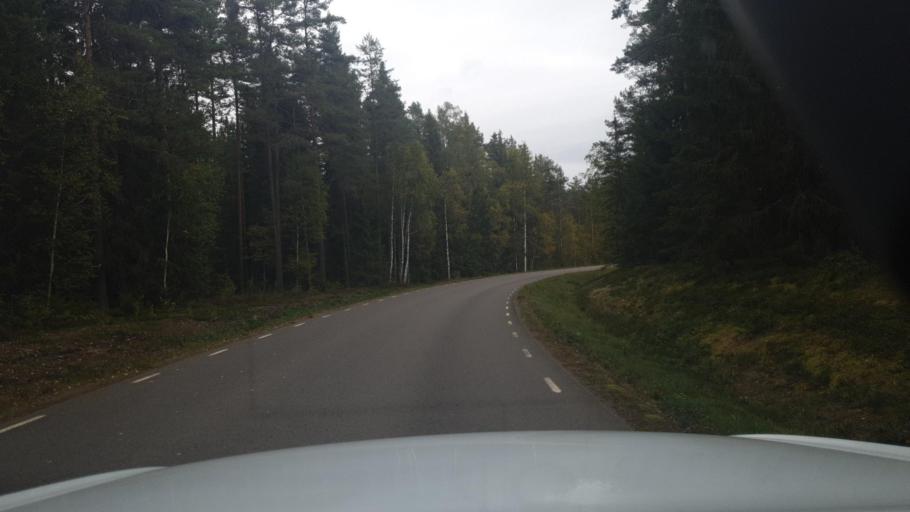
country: SE
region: Vaermland
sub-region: Eda Kommun
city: Charlottenberg
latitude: 60.0158
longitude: 12.6435
